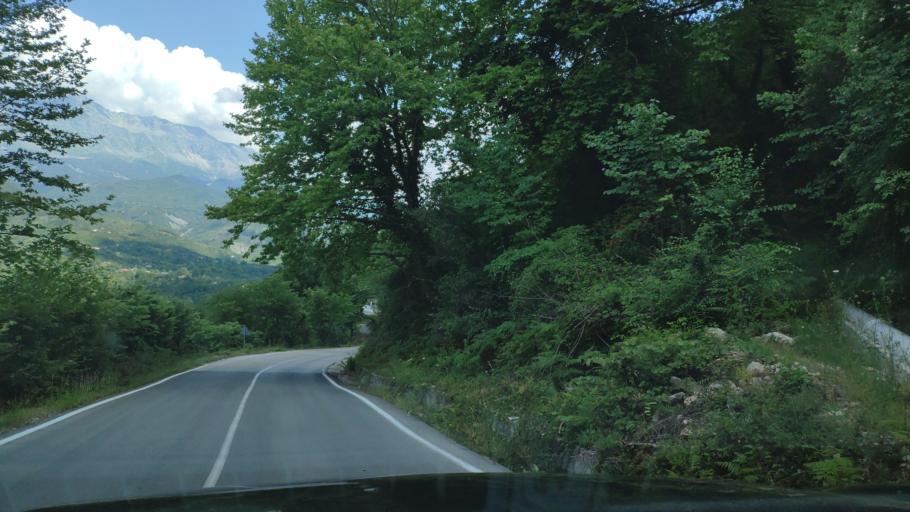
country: GR
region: Epirus
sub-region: Nomos Artas
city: Agios Dimitrios
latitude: 39.4622
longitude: 21.0244
